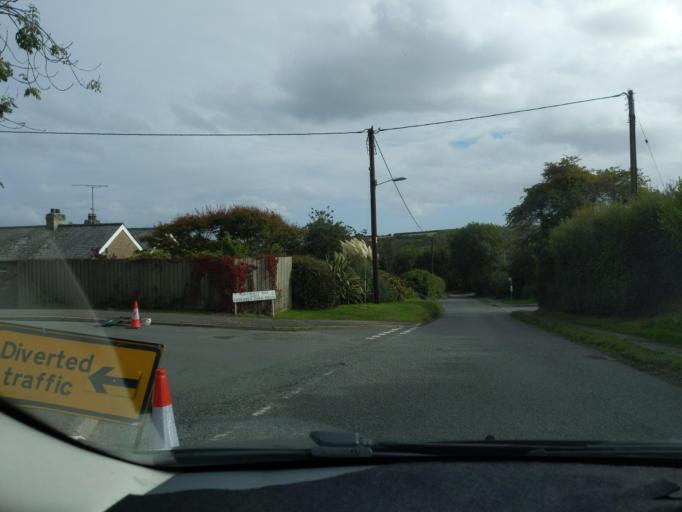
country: GB
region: England
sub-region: Cornwall
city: Mevagissey
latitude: 50.2421
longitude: -4.7988
